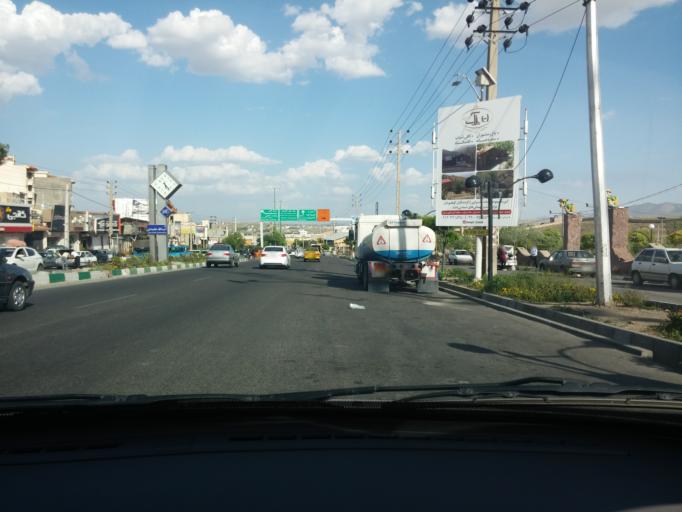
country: IR
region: Tehran
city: Damavand
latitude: 35.6875
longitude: 52.0136
